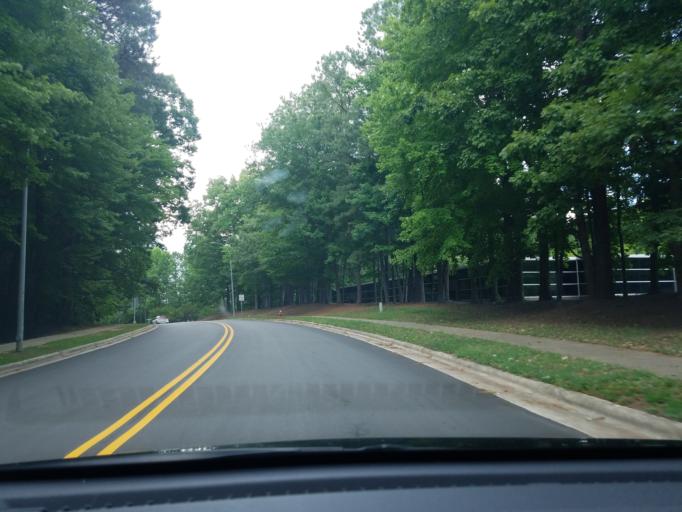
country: US
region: North Carolina
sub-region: Wake County
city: Apex
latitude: 35.7331
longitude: -78.8045
